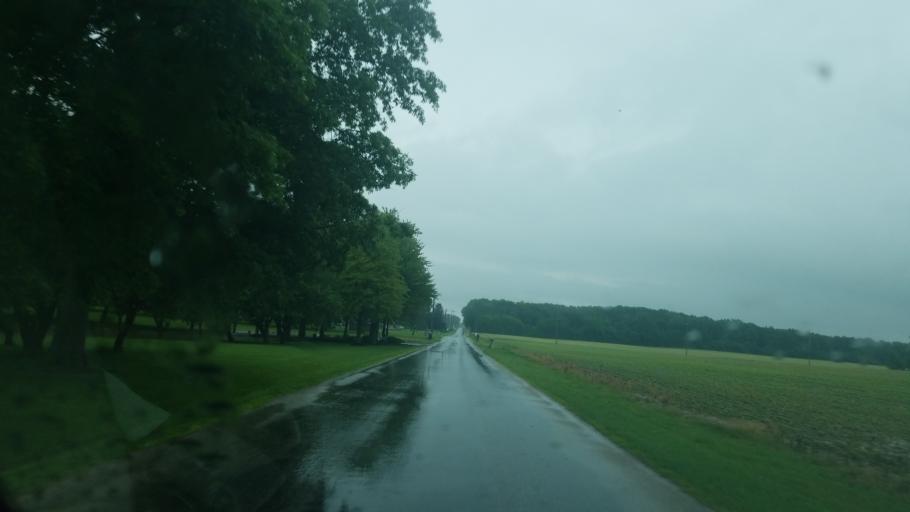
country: US
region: Ohio
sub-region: Huron County
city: Plymouth
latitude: 40.9449
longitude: -82.6901
